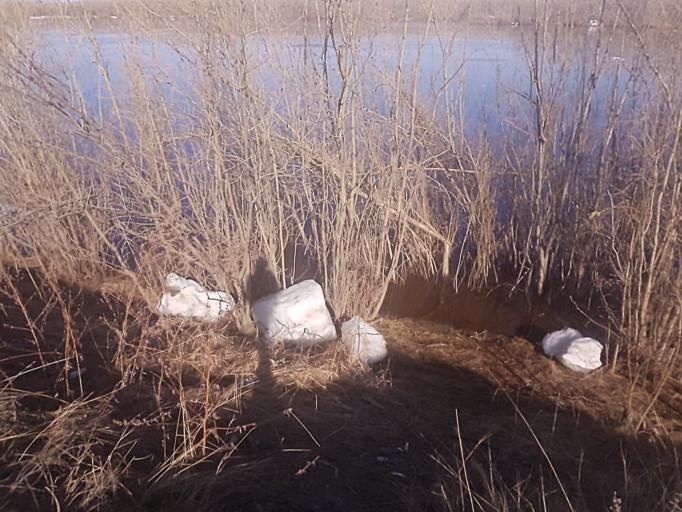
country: RU
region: Sakha
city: Yakutsk
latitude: 61.9722
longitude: 129.7003
